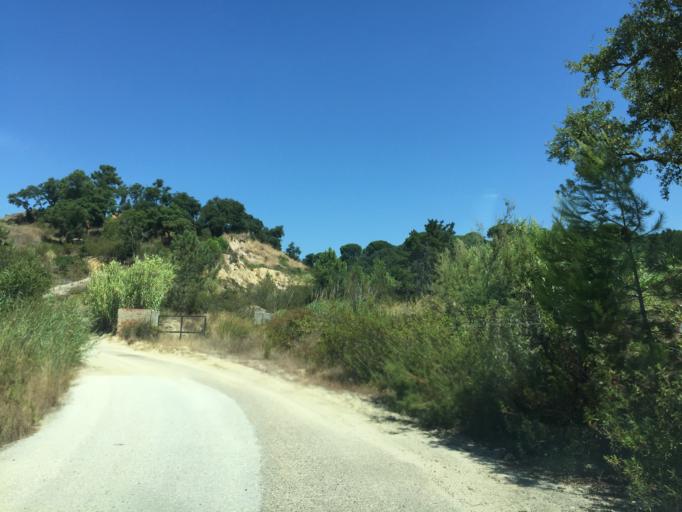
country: PT
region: Lisbon
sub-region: Alenquer
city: Carregado
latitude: 39.0487
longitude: -8.9272
